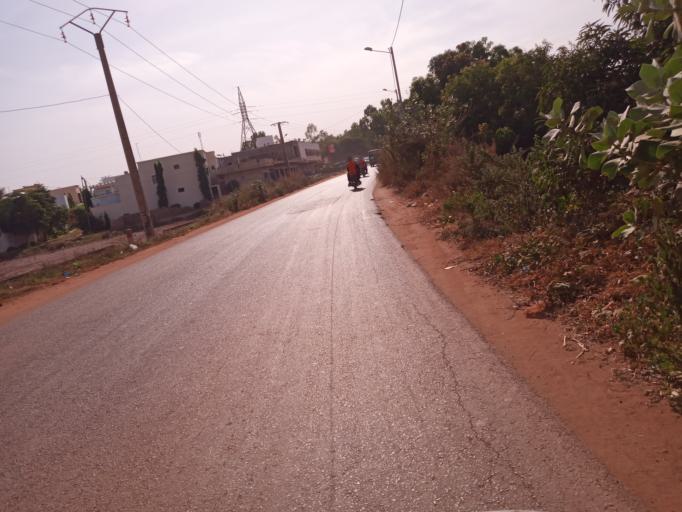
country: ML
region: Bamako
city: Bamako
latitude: 12.6298
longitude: -7.9455
